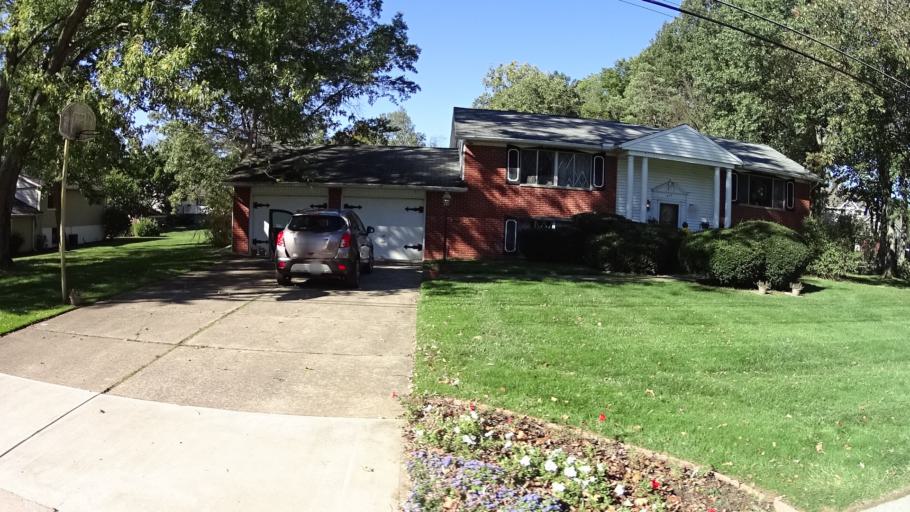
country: US
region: Ohio
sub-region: Lorain County
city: Amherst
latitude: 41.3917
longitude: -82.2434
